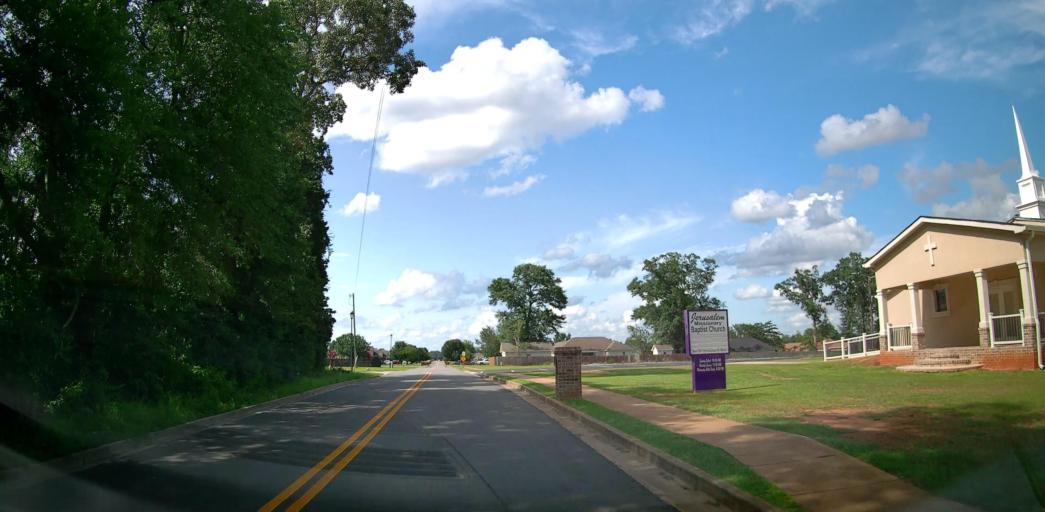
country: US
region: Georgia
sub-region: Houston County
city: Centerville
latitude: 32.5732
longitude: -83.7004
